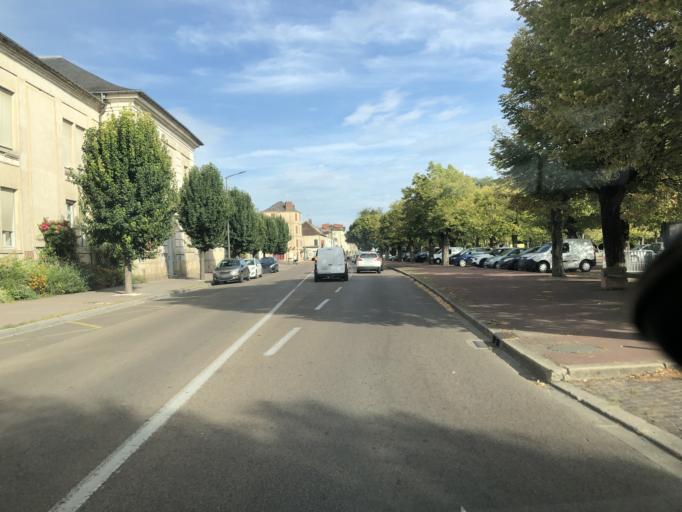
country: FR
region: Bourgogne
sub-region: Departement de l'Yonne
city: Joigny
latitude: 47.9809
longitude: 3.3994
